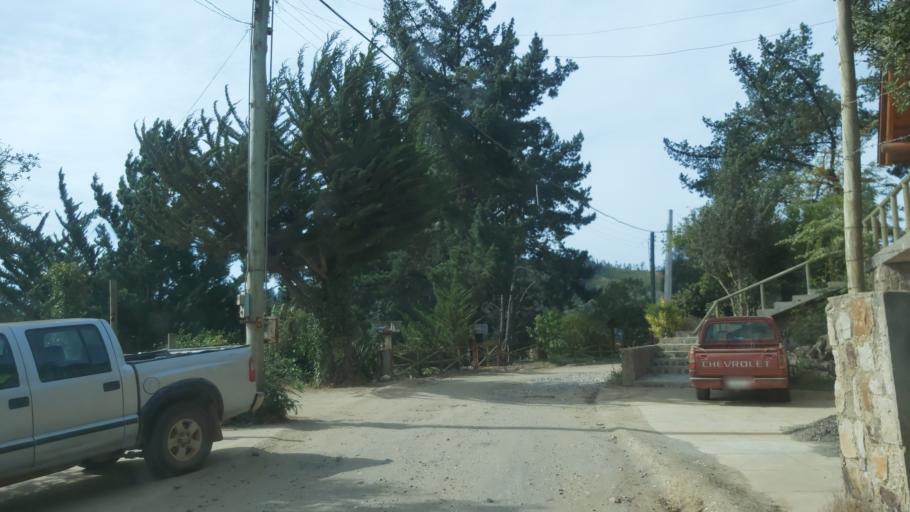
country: CL
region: Maule
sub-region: Provincia de Talca
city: Constitucion
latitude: -34.8409
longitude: -72.0415
